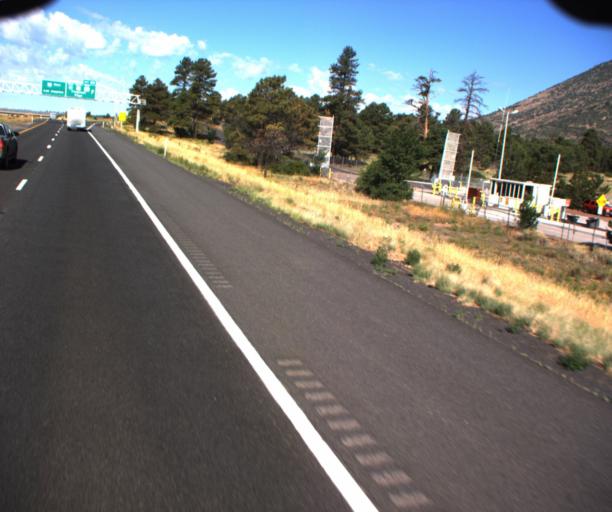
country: US
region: Arizona
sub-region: Coconino County
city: Flagstaff
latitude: 35.2182
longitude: -111.5763
